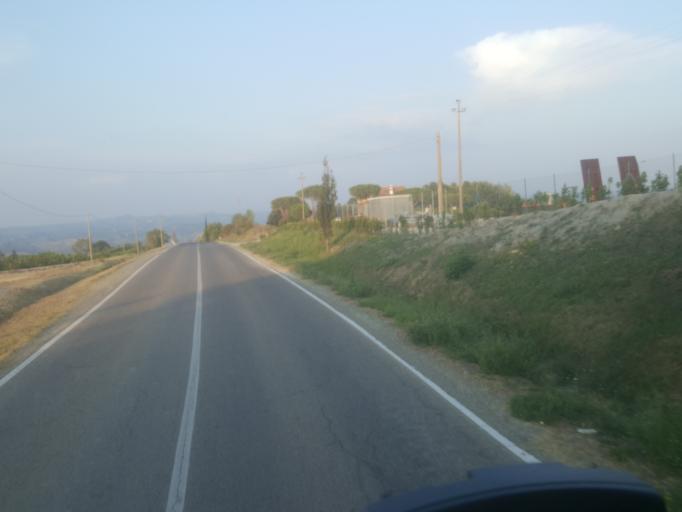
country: IT
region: Tuscany
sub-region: Province of Florence
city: Gambassi Terme
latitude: 43.5446
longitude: 10.9761
